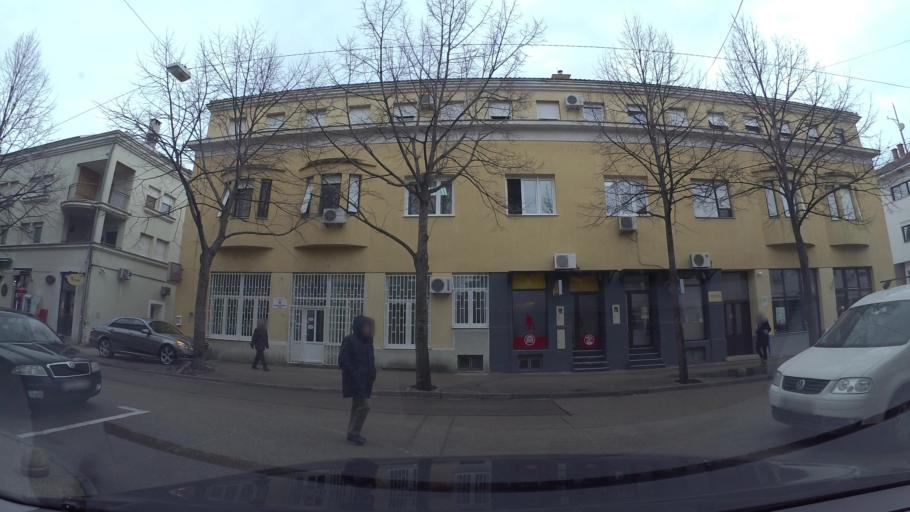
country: BA
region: Federation of Bosnia and Herzegovina
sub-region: Hercegovacko-Bosanski Kanton
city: Mostar
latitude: 43.3425
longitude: 17.8094
